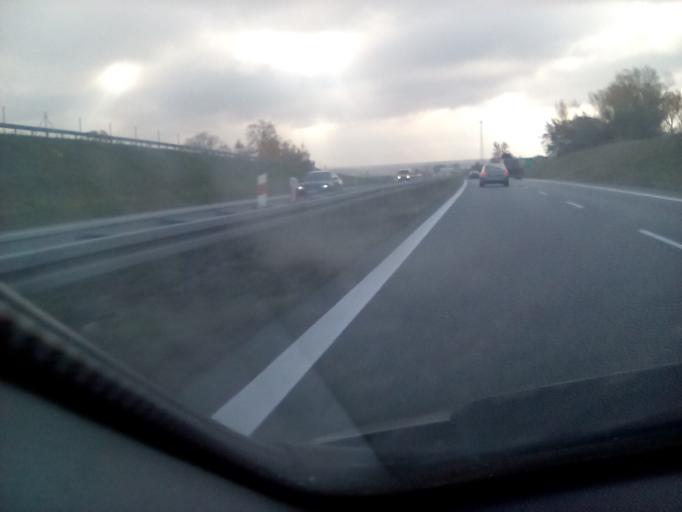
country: PL
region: Masovian Voivodeship
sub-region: Powiat bialobrzeski
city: Promna
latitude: 51.6820
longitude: 20.9382
